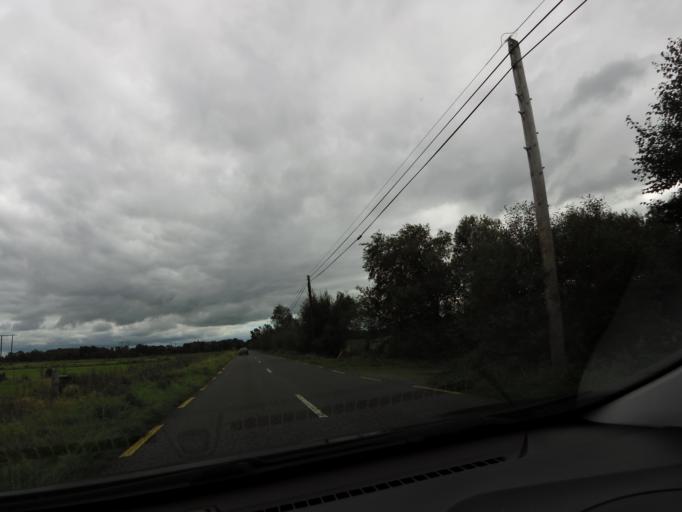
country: IE
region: Leinster
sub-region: Uibh Fhaili
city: Banagher
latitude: 53.2829
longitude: -8.0712
